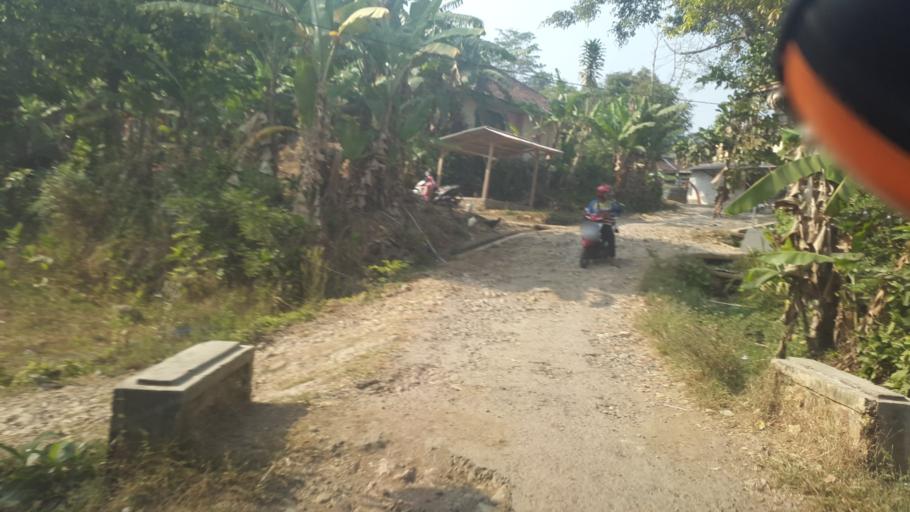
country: ID
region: West Java
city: Suryabakti
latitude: -7.0172
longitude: 106.8454
